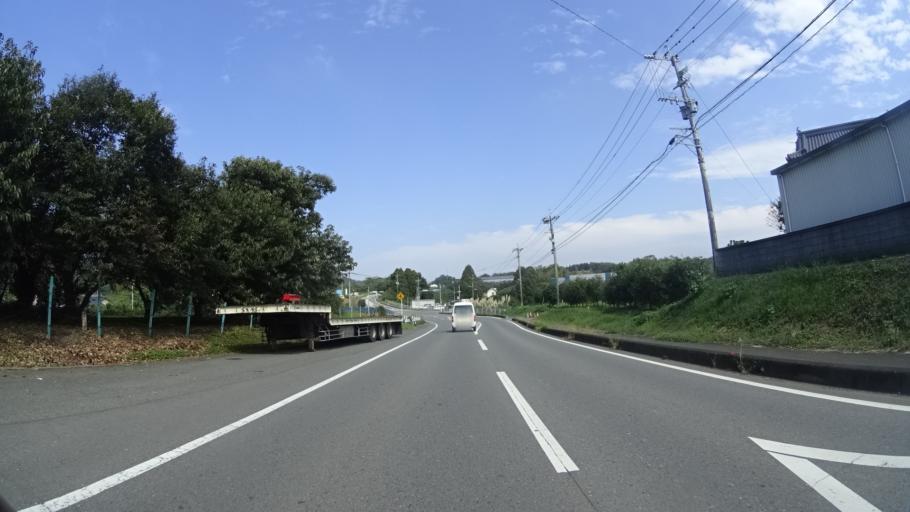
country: JP
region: Kumamoto
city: Matsubase
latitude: 32.6657
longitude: 130.7182
